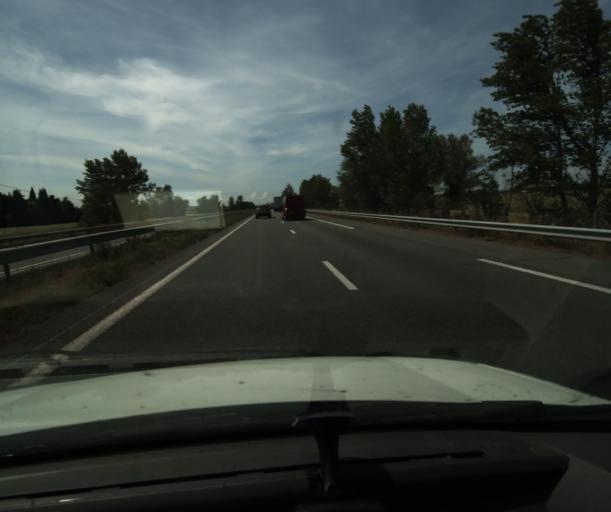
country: FR
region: Languedoc-Roussillon
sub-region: Departement de l'Aude
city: Saint-Martin-Lalande
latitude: 43.2566
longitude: 2.0349
